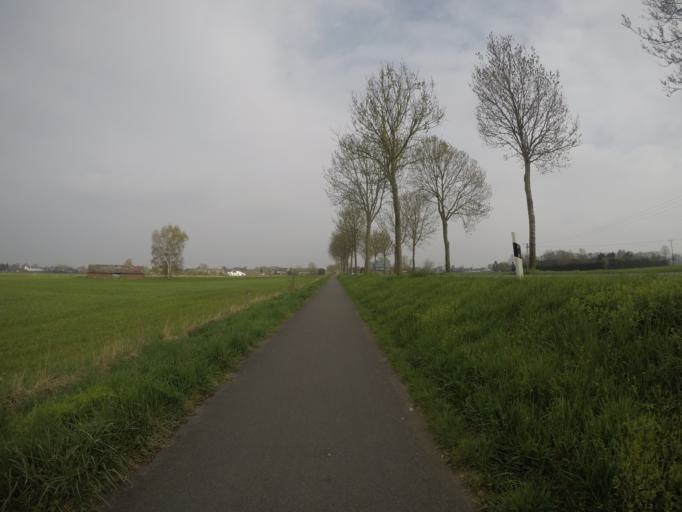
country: DE
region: North Rhine-Westphalia
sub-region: Regierungsbezirk Munster
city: Isselburg
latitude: 51.8543
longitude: 6.5035
